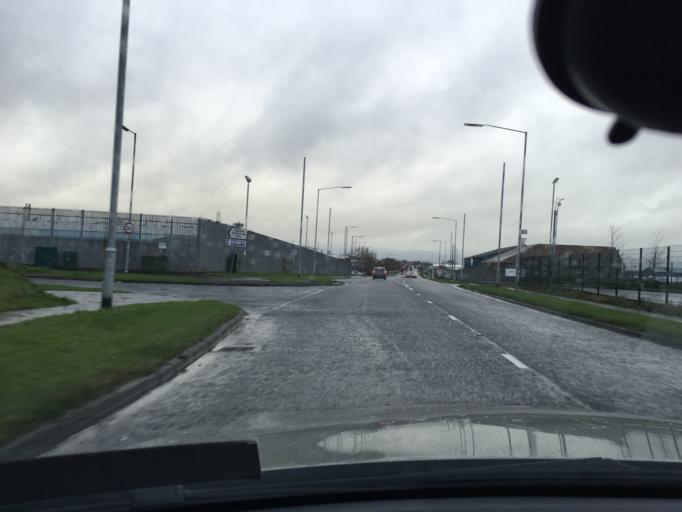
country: GB
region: Northern Ireland
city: Carnmoney
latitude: 54.6730
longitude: -5.9794
